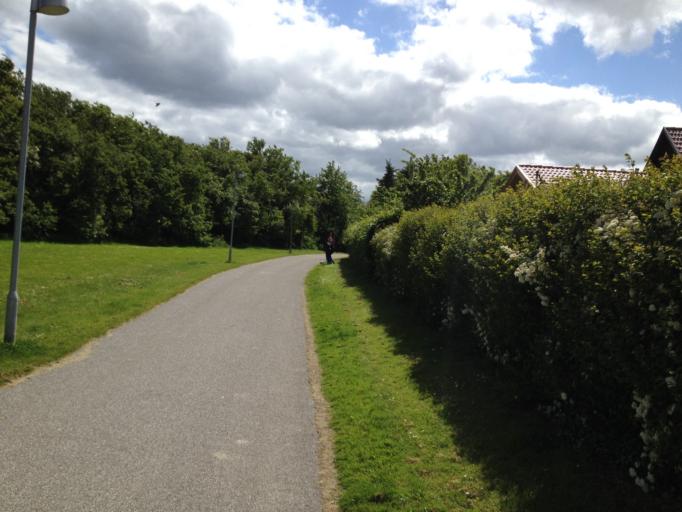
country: DK
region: Capital Region
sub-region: Fredensborg Kommune
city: Niva
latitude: 55.9422
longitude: 12.4951
